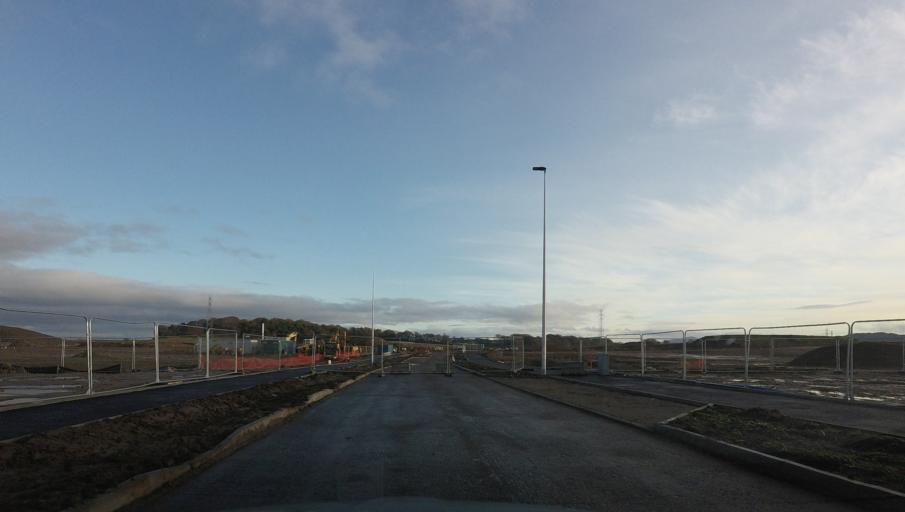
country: GB
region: Scotland
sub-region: West Lothian
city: Kirknewton
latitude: 55.9024
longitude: -3.4382
